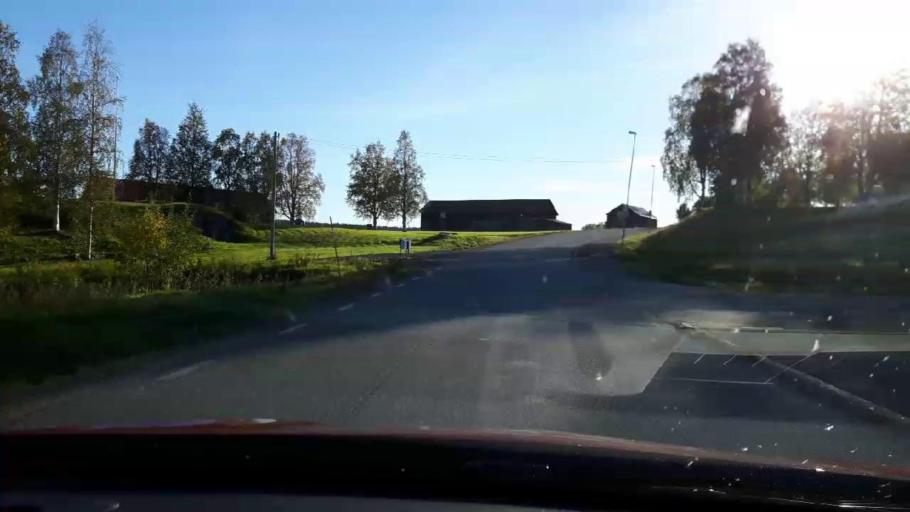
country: SE
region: Jaemtland
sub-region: OEstersunds Kommun
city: Lit
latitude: 63.8146
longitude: 14.8056
